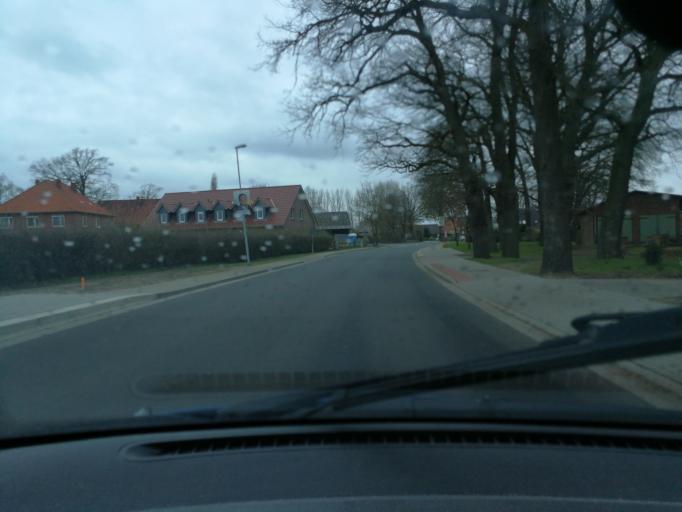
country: DE
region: Lower Saxony
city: Wittorf
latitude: 53.3304
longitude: 10.3807
